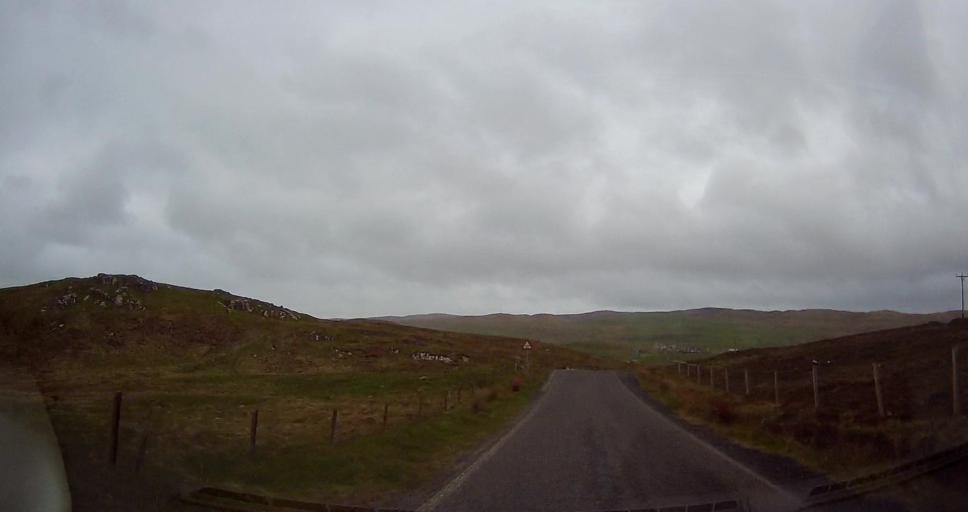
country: GB
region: Scotland
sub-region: Shetland Islands
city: Lerwick
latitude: 60.3801
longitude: -1.3809
